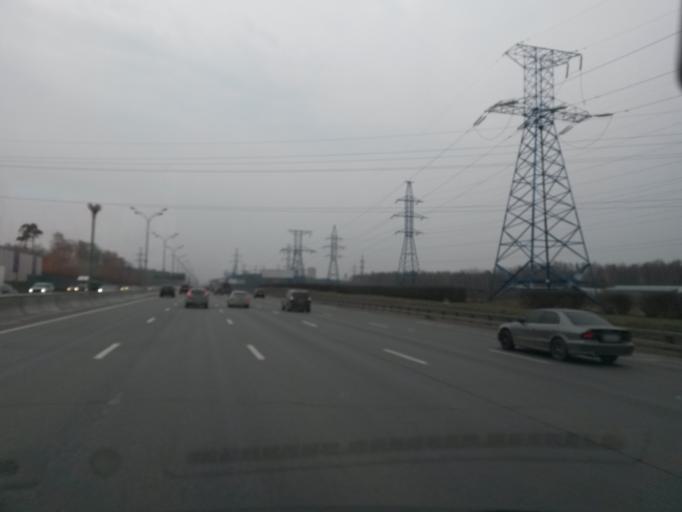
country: RU
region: Moscow
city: Ivanovskoye
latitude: 55.7820
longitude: 37.8423
